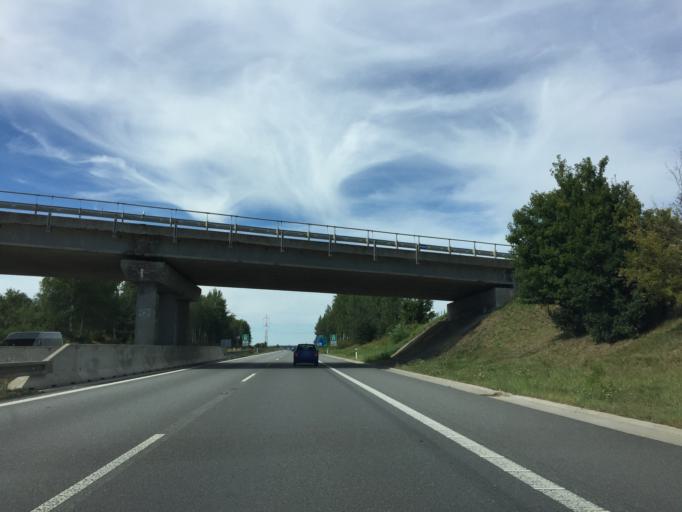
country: CZ
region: Jihocesky
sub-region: Okres Tabor
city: Sezimovo Usti
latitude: 49.4223
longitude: 14.7033
